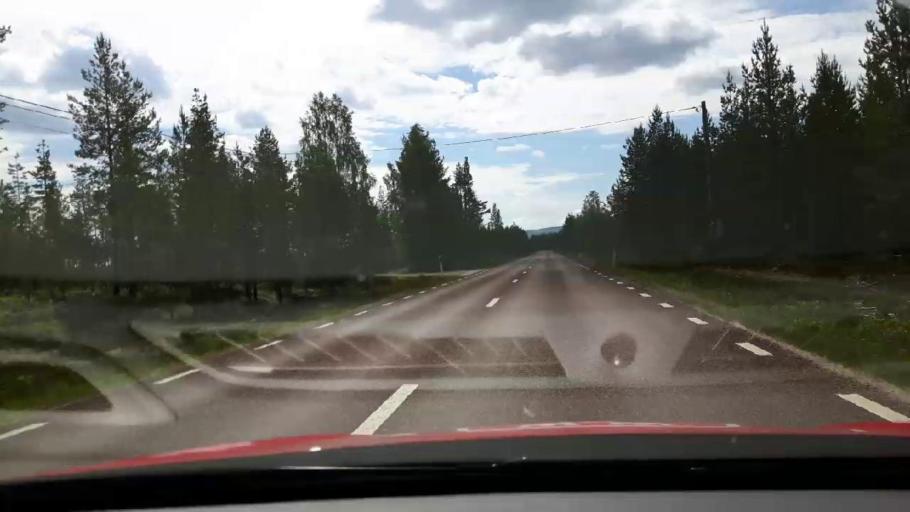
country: SE
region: Jaemtland
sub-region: Harjedalens Kommun
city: Sveg
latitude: 62.1244
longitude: 14.9711
